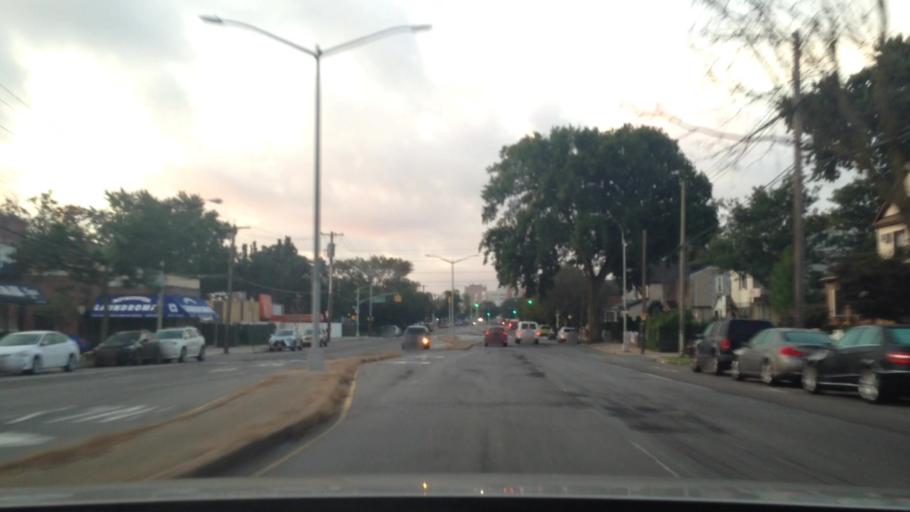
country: US
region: New York
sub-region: Queens County
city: Jamaica
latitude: 40.7270
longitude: -73.8052
